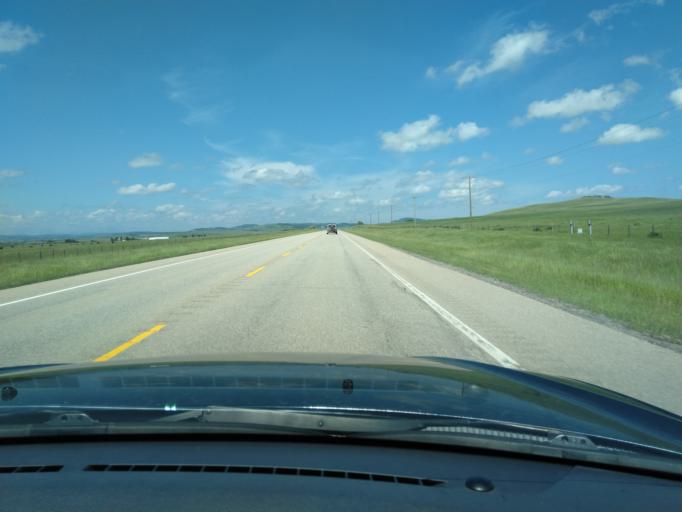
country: CA
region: Alberta
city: Cochrane
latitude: 51.2125
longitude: -114.5286
